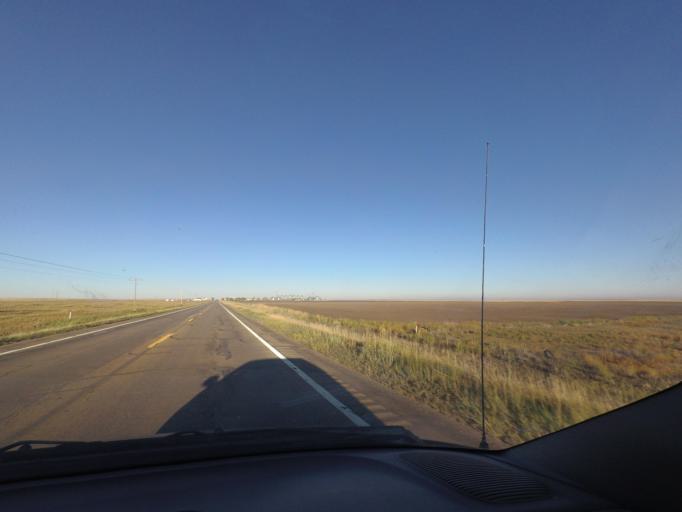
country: US
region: Colorado
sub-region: Washington County
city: Akron
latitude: 39.7414
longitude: -103.2025
